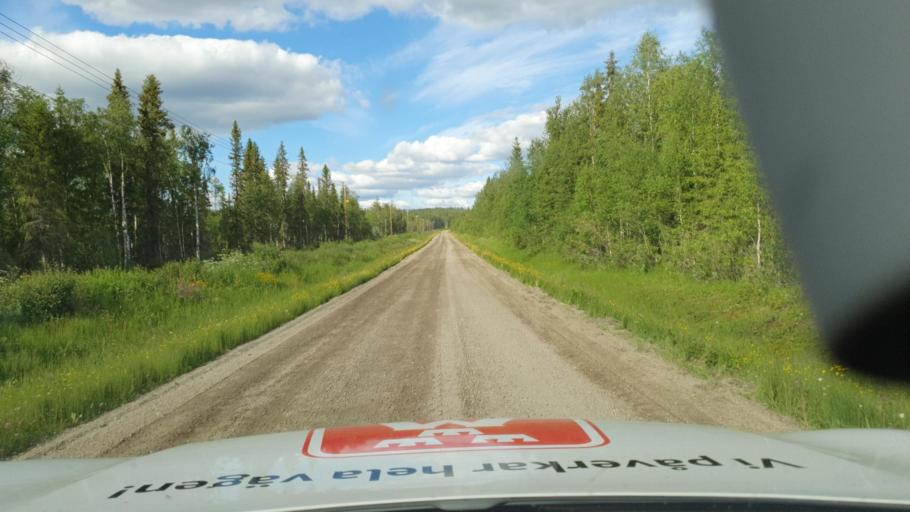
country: SE
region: Vaesterbotten
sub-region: Lycksele Kommun
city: Lycksele
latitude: 64.3228
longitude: 18.3442
